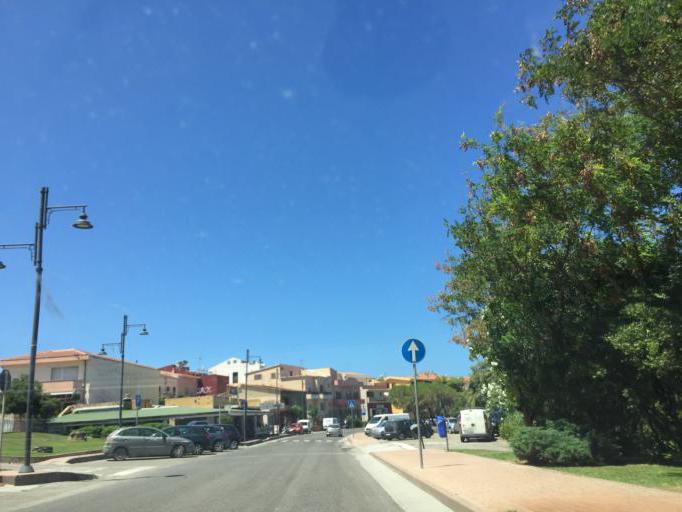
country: IT
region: Sardinia
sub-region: Provincia di Sassari
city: Castelsardo
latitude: 40.9115
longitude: 8.7192
